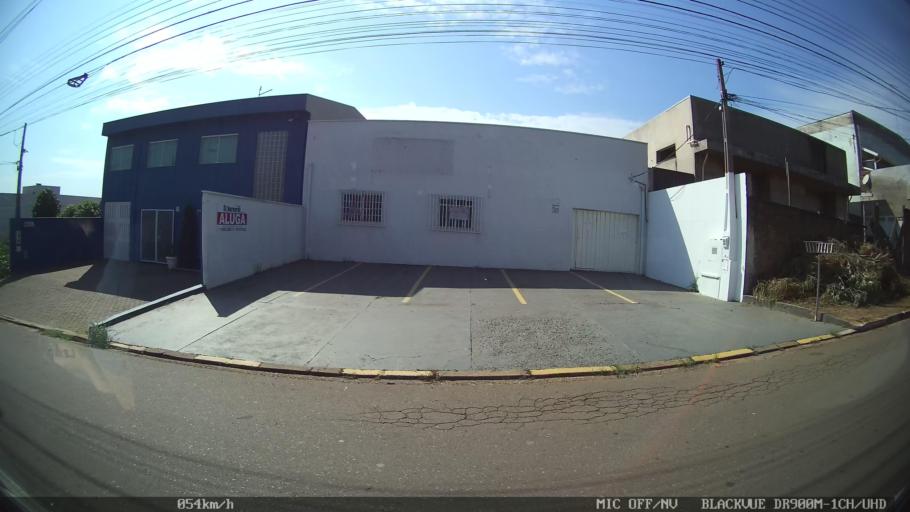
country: BR
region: Sao Paulo
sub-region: Paulinia
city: Paulinia
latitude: -22.7803
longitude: -47.1627
